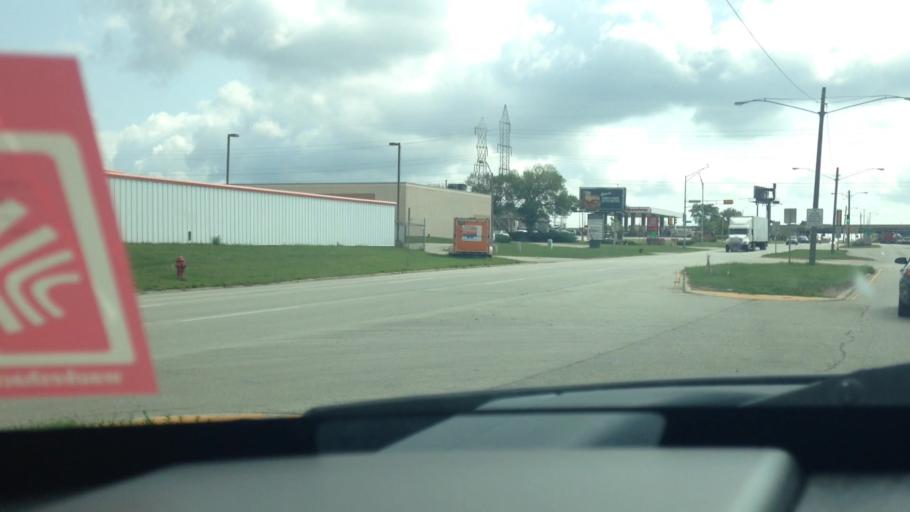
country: US
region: Wisconsin
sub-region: Waukesha County
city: Butler
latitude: 43.1170
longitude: -88.0627
